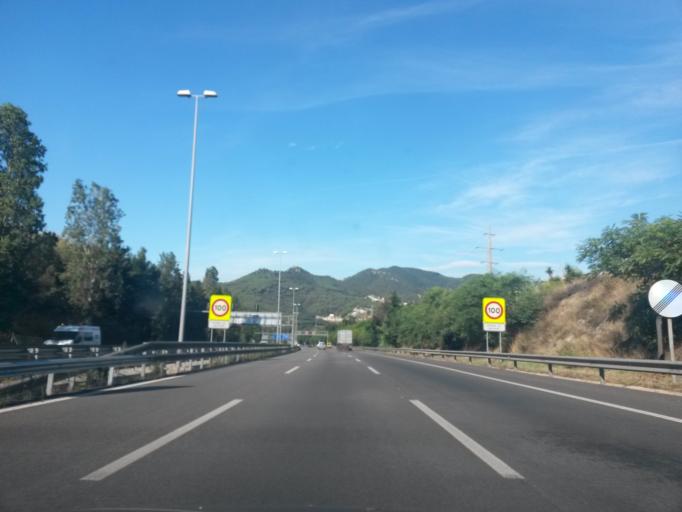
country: ES
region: Catalonia
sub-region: Provincia de Barcelona
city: Mataro
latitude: 41.5504
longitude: 2.4244
